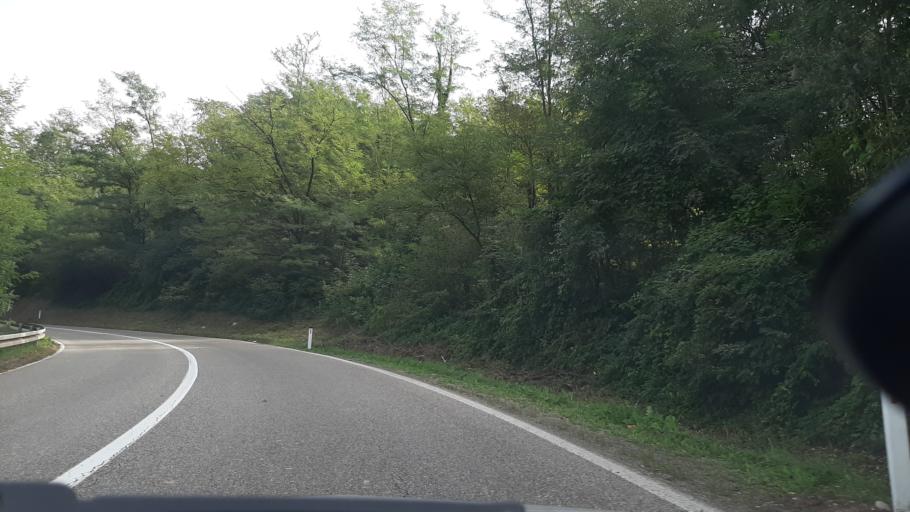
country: BA
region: Republika Srpska
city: Laktasi
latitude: 44.8739
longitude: 17.3593
